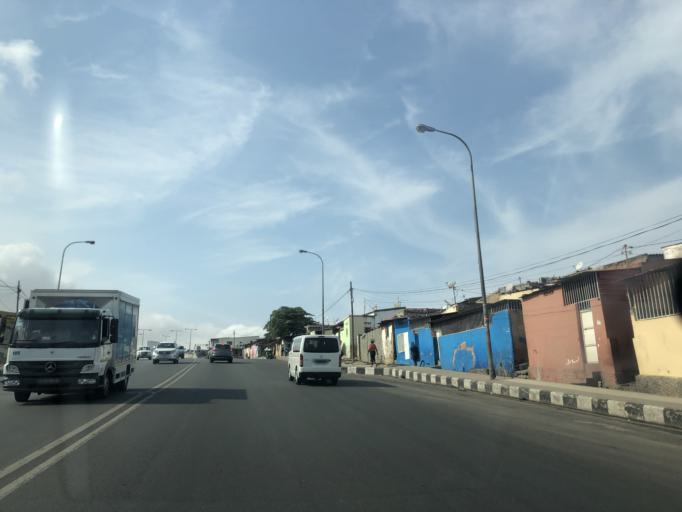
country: AO
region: Luanda
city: Luanda
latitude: -8.8315
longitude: 13.2256
